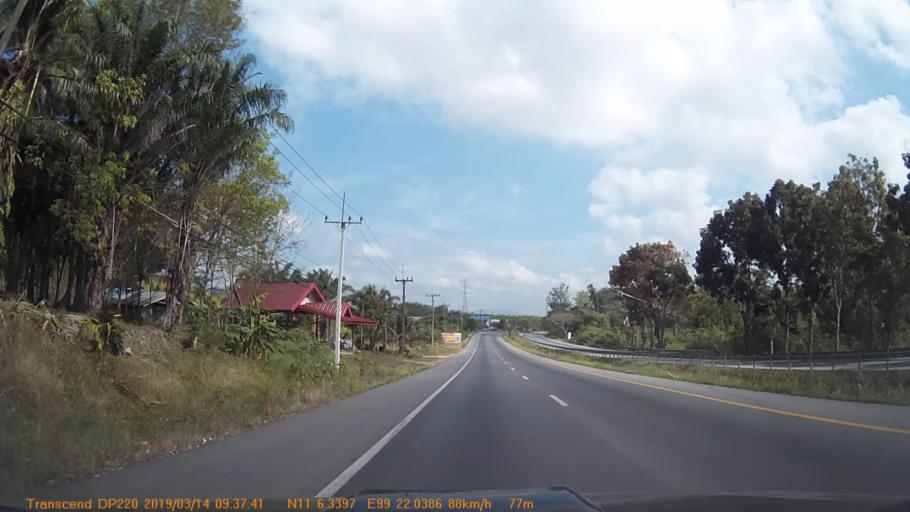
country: TH
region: Prachuap Khiri Khan
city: Bang Saphan Noi
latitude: 11.1059
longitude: 99.3673
